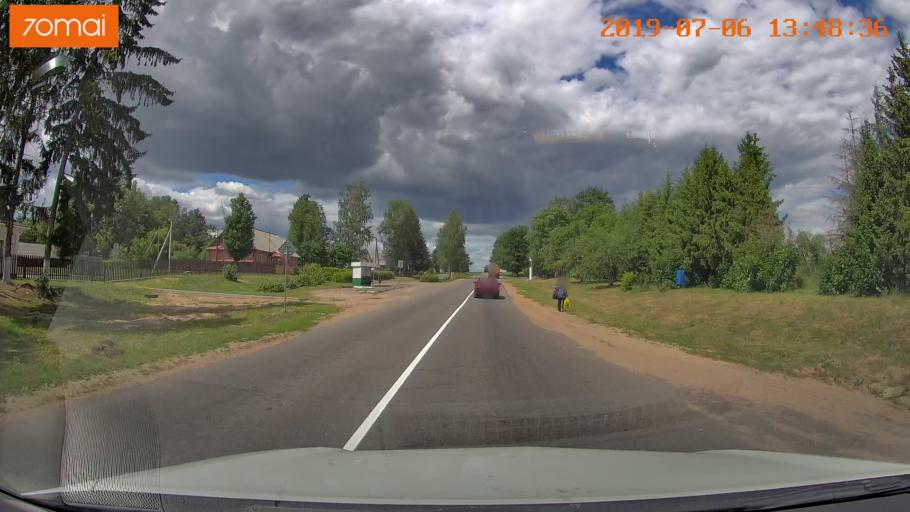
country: BY
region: Minsk
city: Enyerhyetykaw
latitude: 53.6909
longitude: 26.8561
